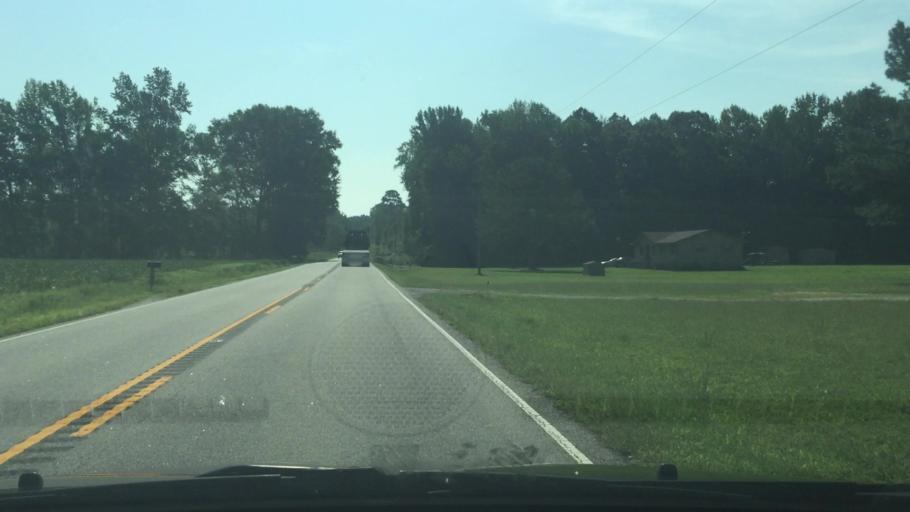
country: US
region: Virginia
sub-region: Sussex County
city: Sussex
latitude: 36.9765
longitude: -77.2106
